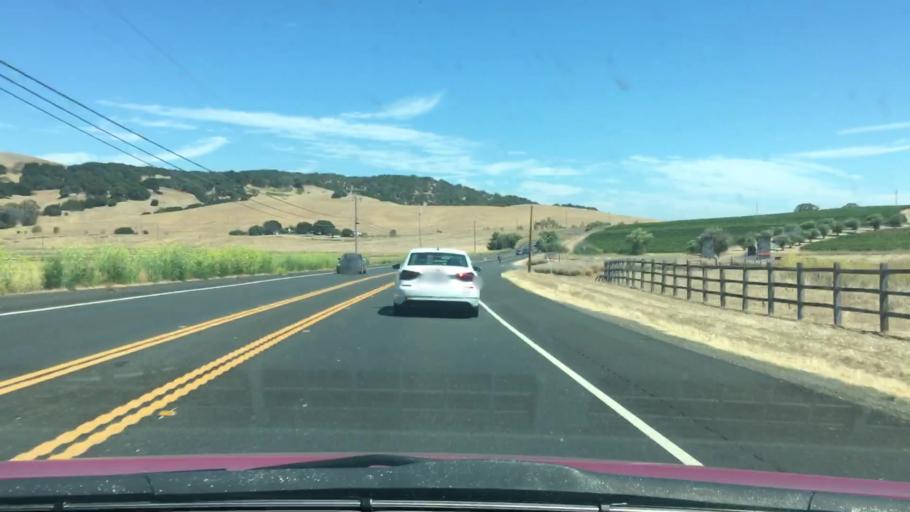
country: US
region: California
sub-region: Marin County
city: Black Point-Green Point
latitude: 38.1709
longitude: -122.4559
